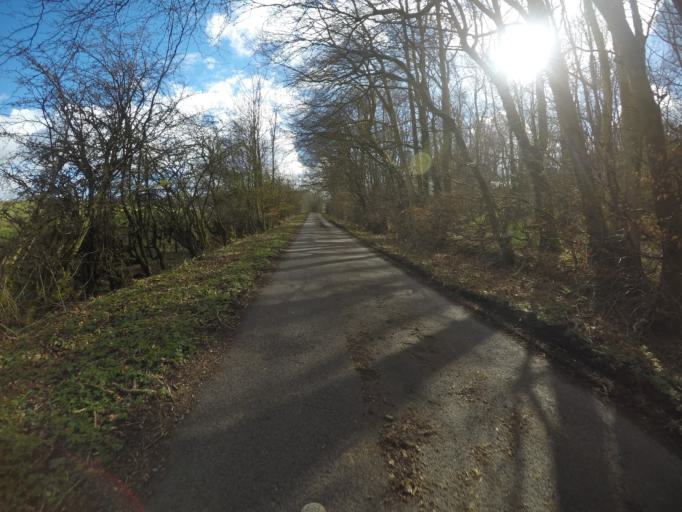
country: GB
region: Scotland
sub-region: North Ayrshire
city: Beith
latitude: 55.7153
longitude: -4.6392
